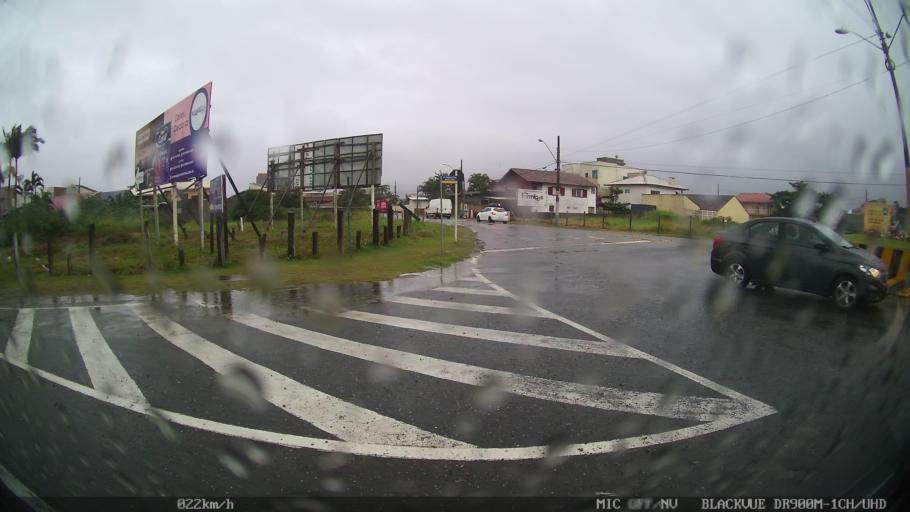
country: BR
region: Santa Catarina
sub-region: Navegantes
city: Navegantes
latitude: -26.8805
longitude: -48.6411
